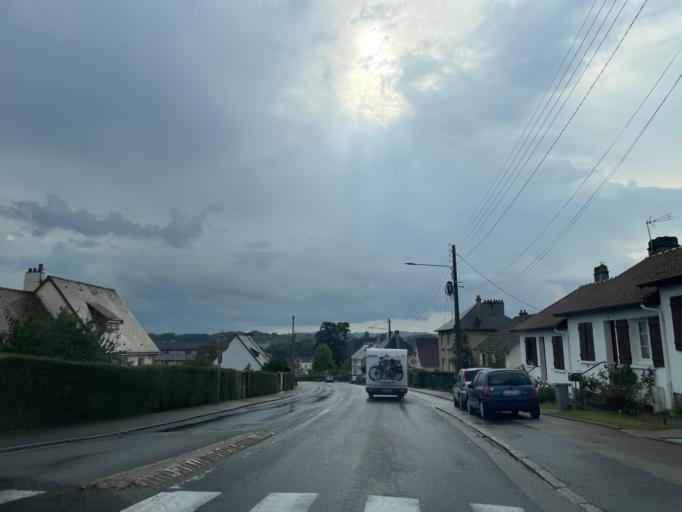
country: FR
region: Haute-Normandie
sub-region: Departement de la Seine-Maritime
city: Neufchatel-en-Bray
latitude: 49.7377
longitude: 1.4385
